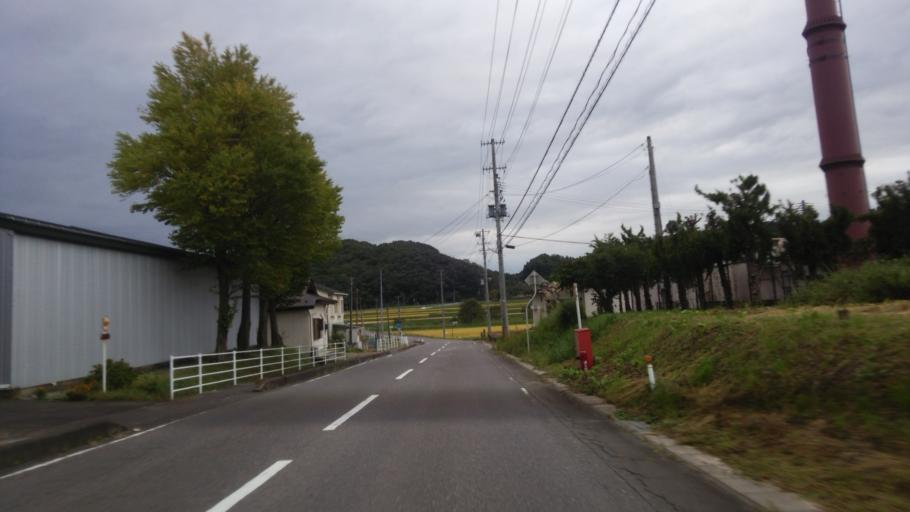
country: JP
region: Fukushima
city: Sukagawa
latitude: 37.2544
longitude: 140.2480
